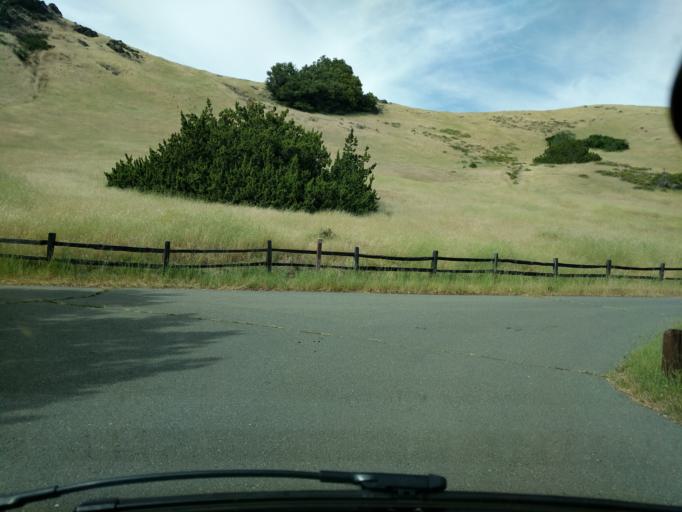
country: US
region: California
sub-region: Contra Costa County
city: Diablo
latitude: 37.8786
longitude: -121.9336
